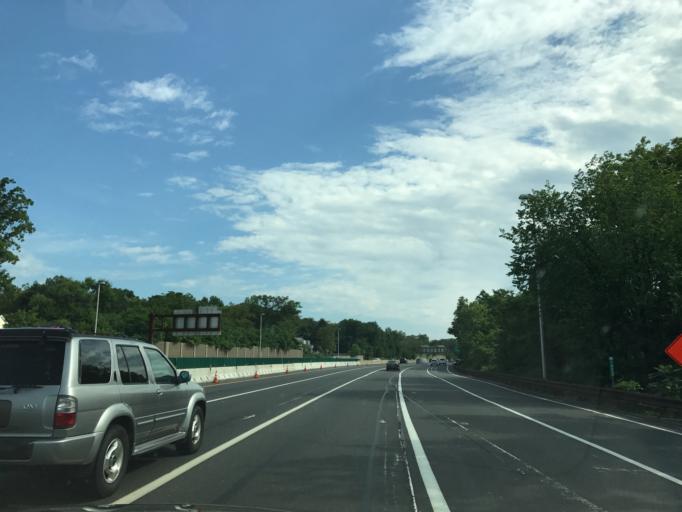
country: US
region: New Jersey
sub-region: Union County
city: Hillside
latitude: 40.7113
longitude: -74.2441
